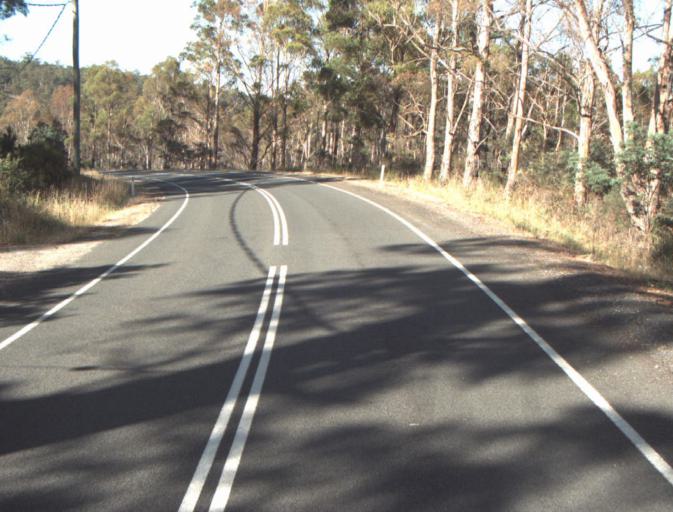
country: AU
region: Tasmania
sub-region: Launceston
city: Newstead
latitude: -41.3956
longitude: 147.2932
